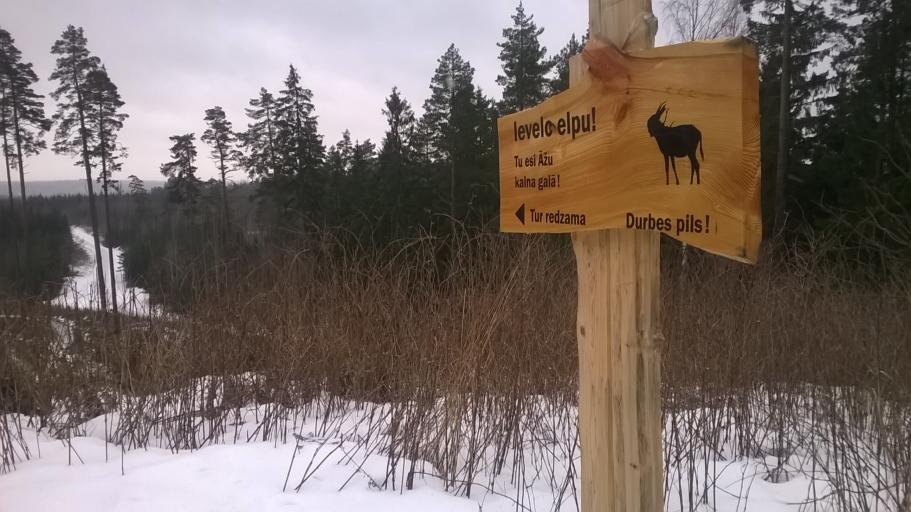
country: LV
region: Tukuma Rajons
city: Tukums
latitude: 56.9981
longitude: 23.1721
